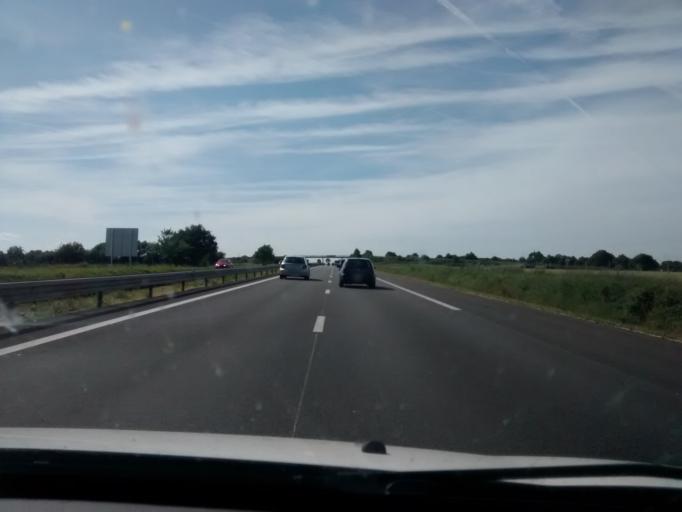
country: FR
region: Pays de la Loire
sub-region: Departement de la Sarthe
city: Brulon
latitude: 48.0157
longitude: -0.3055
